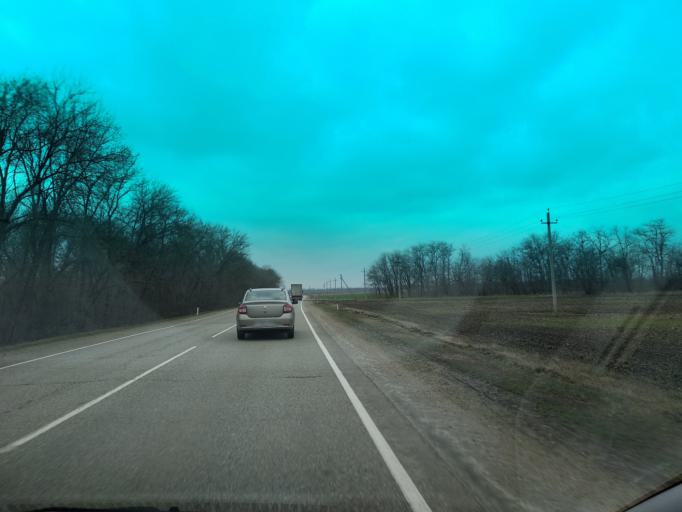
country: RU
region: Krasnodarskiy
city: Novomalorossiyskaya
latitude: 45.7262
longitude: 39.8994
